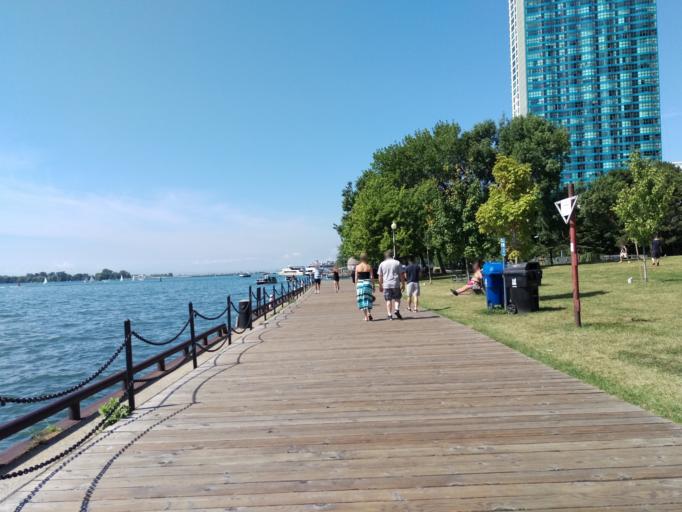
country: CA
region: Ontario
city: Toronto
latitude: 43.6394
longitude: -79.3763
